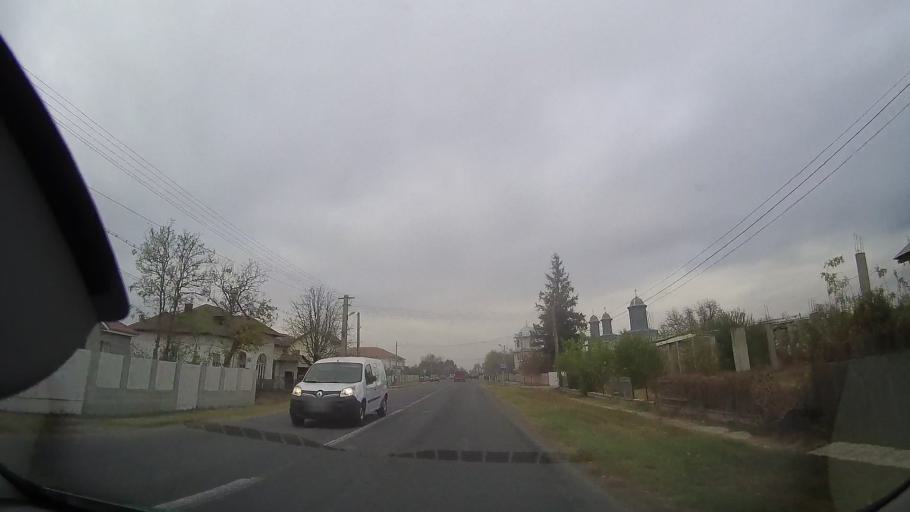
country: RO
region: Buzau
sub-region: Comuna Padina
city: Padina
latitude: 44.8271
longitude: 27.1121
